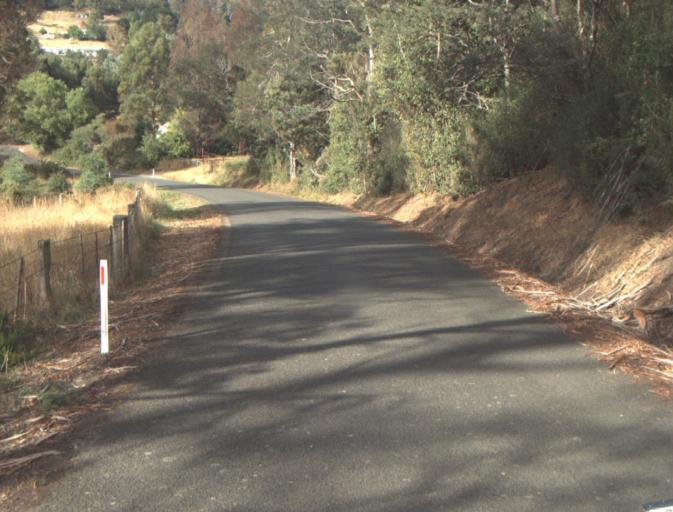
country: AU
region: Tasmania
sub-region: Launceston
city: Mayfield
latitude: -41.2889
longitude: 147.2065
